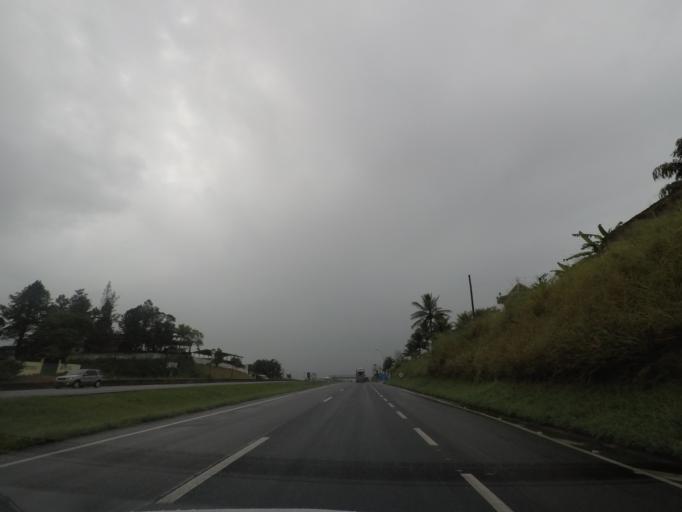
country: BR
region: Sao Paulo
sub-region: Registro
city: Registro
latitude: -24.4631
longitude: -47.8182
